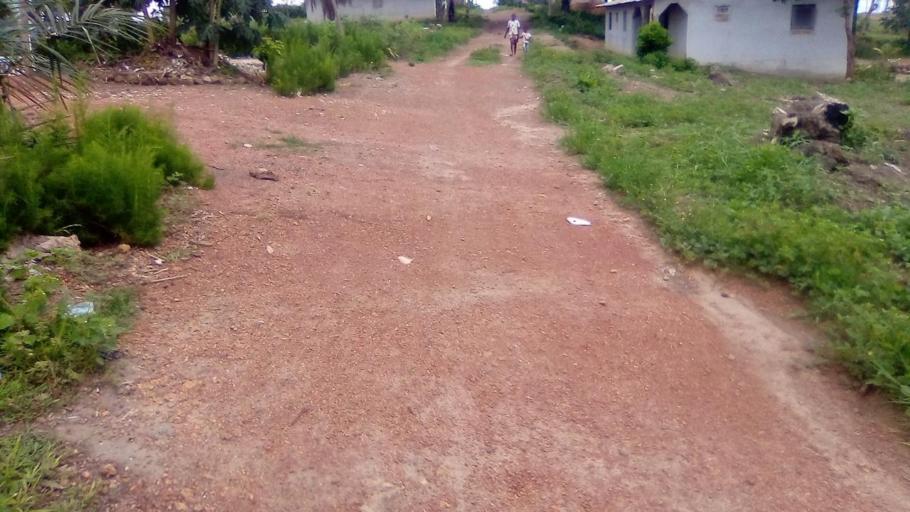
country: SL
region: Southern Province
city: Bo
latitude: 7.9330
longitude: -11.7433
